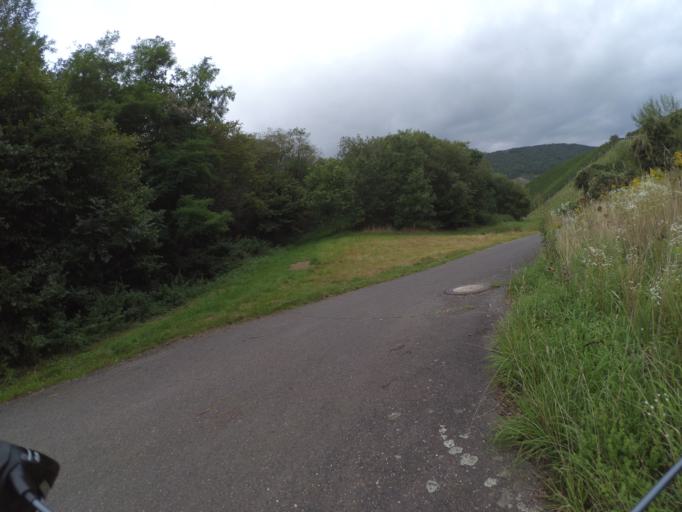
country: DE
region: Rheinland-Pfalz
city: Neumagen-Dhron
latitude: 49.8425
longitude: 6.8990
